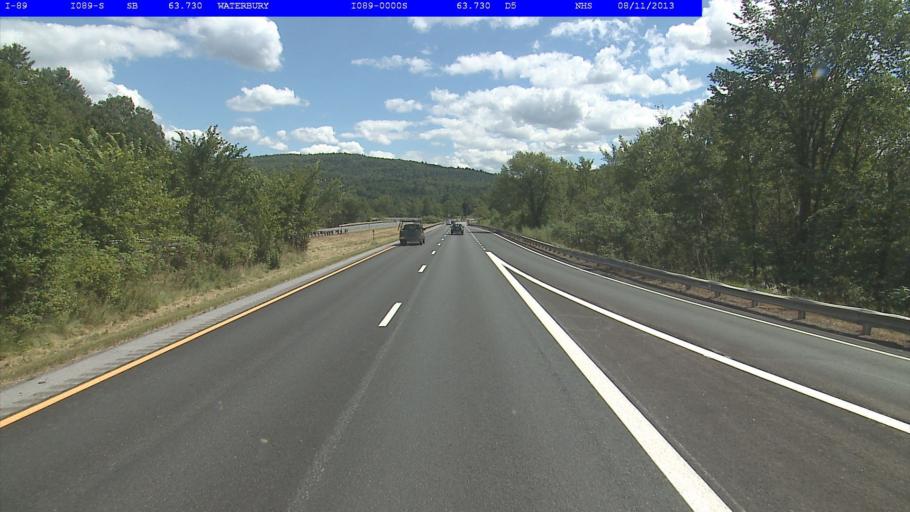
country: US
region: Vermont
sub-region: Washington County
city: Waterbury
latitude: 44.3429
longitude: -72.7520
